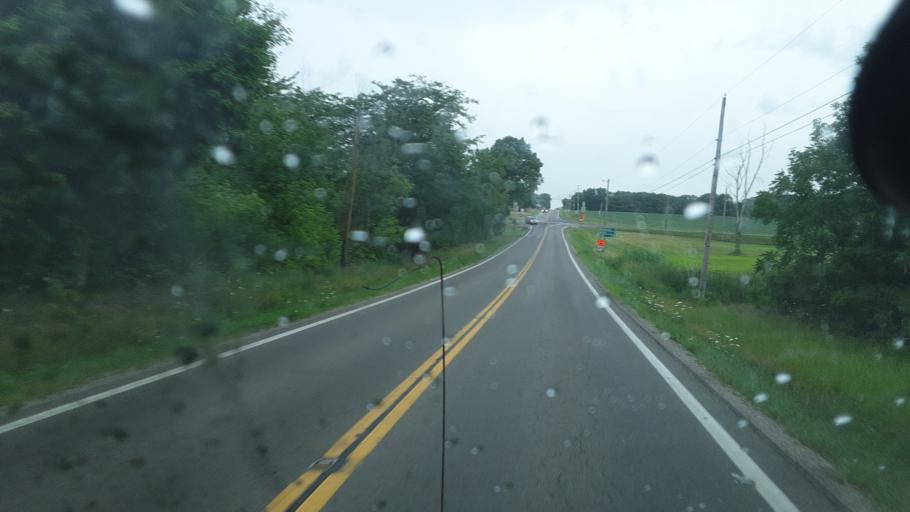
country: US
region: Ohio
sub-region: Williams County
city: Bryan
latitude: 41.4879
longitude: -84.6131
